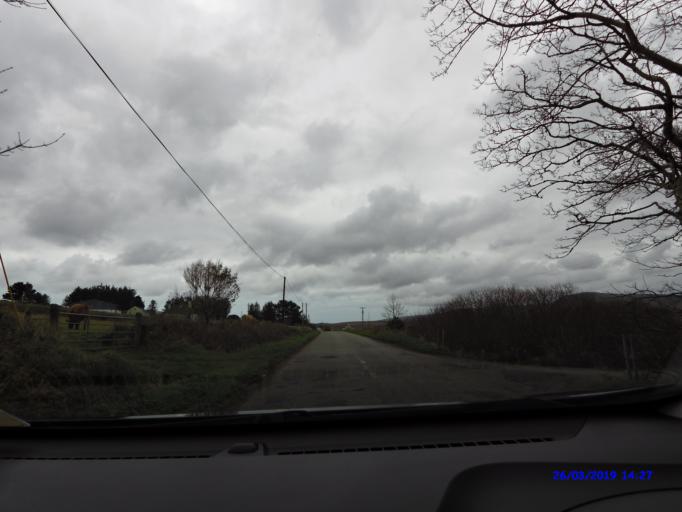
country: IE
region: Connaught
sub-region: Maigh Eo
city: Crossmolina
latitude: 54.2491
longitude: -9.6297
